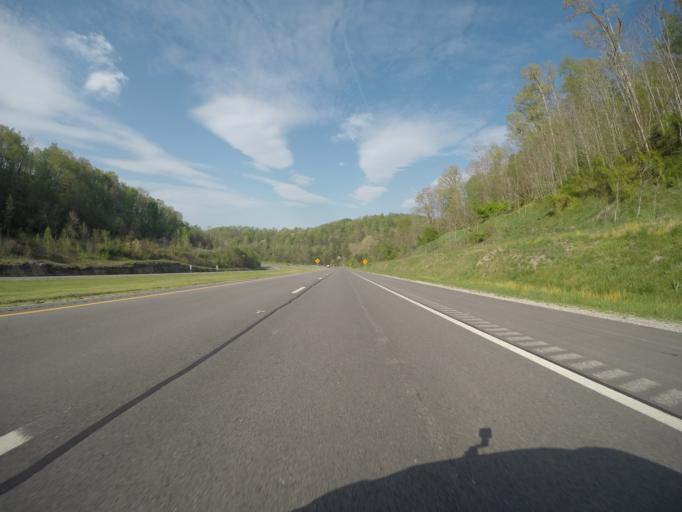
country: US
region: West Virginia
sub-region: Kanawha County
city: Alum Creek
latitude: 38.2909
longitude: -81.7592
